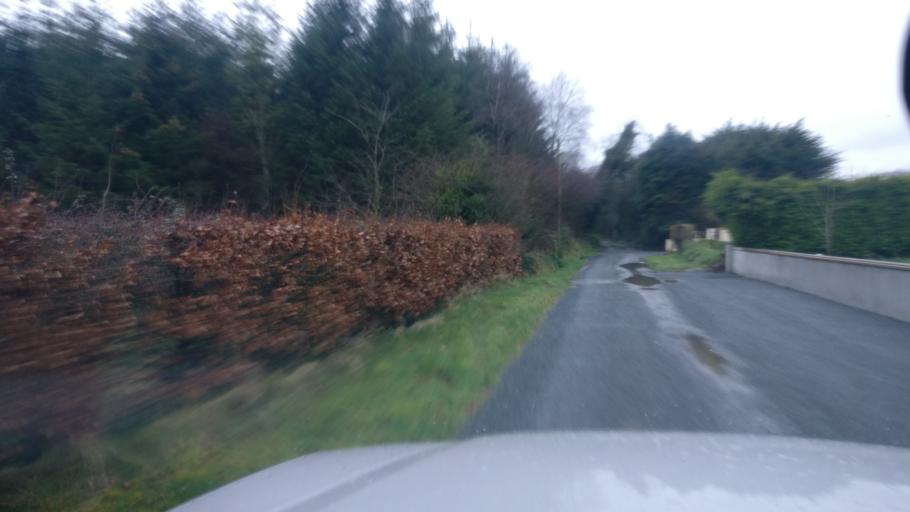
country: IE
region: Connaught
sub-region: County Galway
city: Ballinasloe
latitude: 53.2528
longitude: -8.3636
